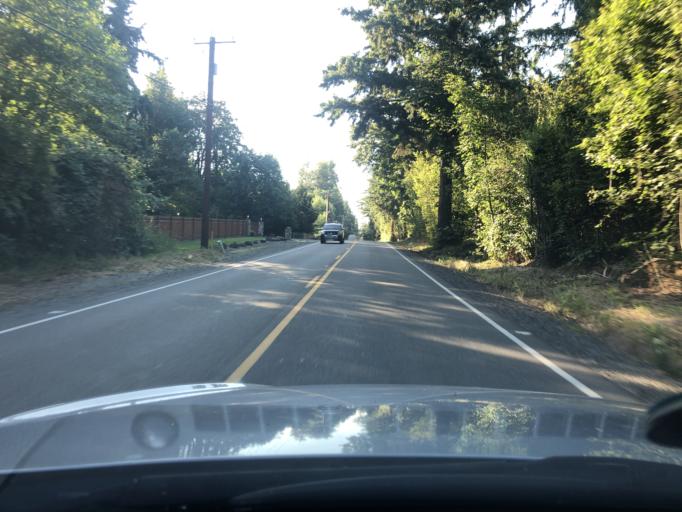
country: US
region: Washington
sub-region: Pierce County
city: Bonney Lake
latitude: 47.2404
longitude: -122.1457
